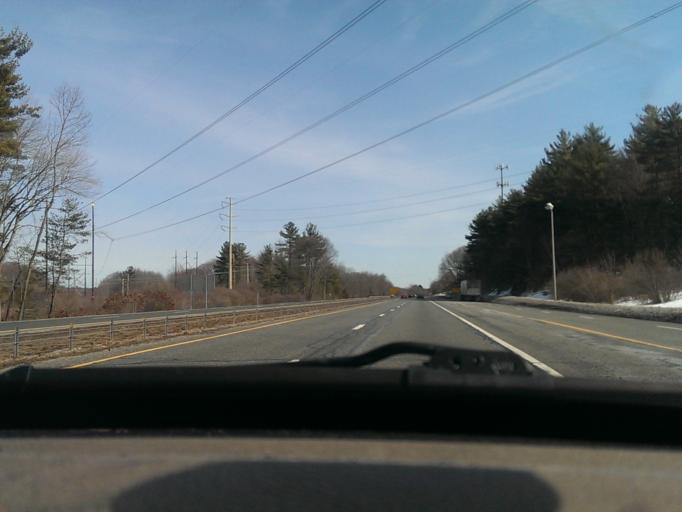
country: US
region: Rhode Island
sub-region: Providence County
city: Woonsocket
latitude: 41.9725
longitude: -71.5179
